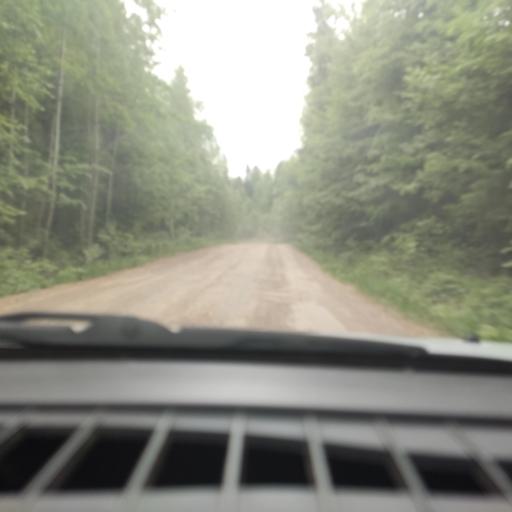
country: RU
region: Perm
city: Novyye Lyady
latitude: 57.9009
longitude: 56.6522
